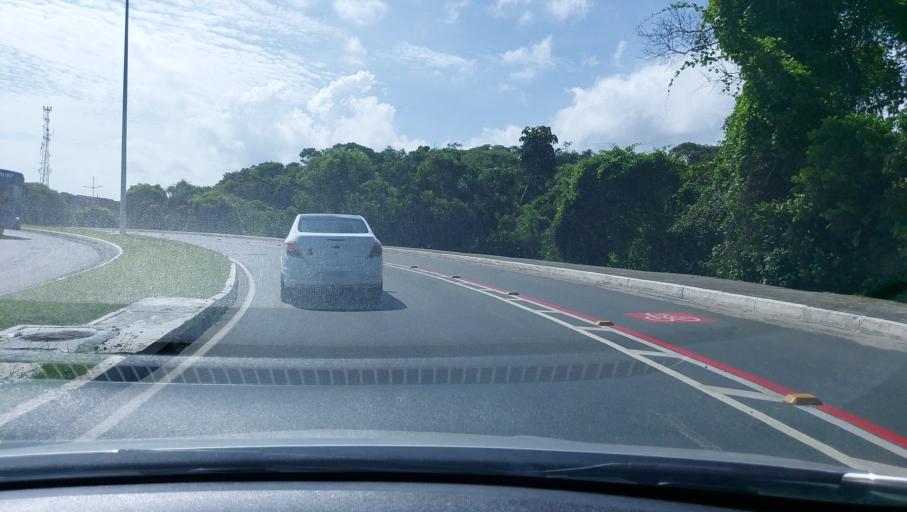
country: BR
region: Bahia
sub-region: Salvador
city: Salvador
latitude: -12.9725
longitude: -38.4496
